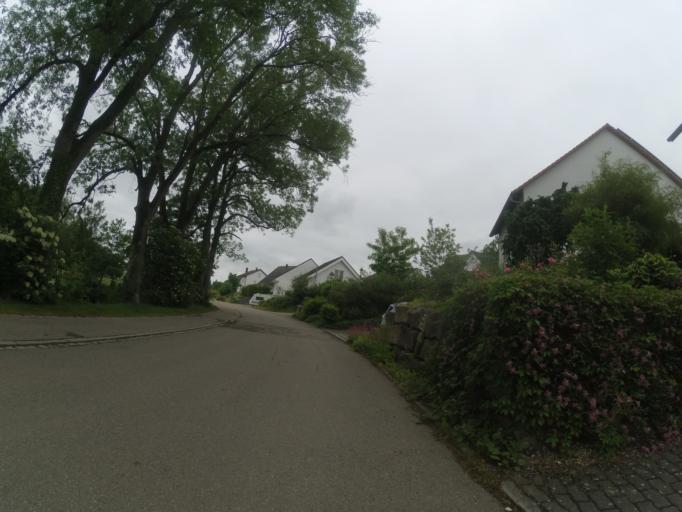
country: DE
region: Baden-Wuerttemberg
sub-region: Tuebingen Region
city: Langenau
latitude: 48.4968
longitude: 10.1058
